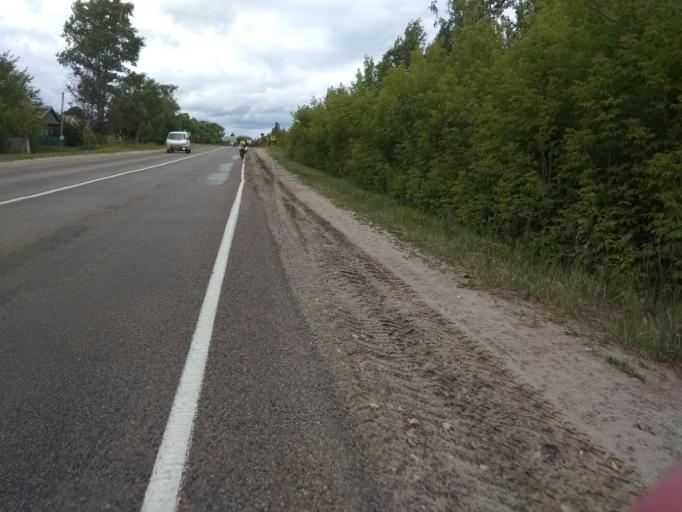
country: RU
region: Moskovskaya
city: Kerva
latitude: 55.5888
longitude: 39.7011
